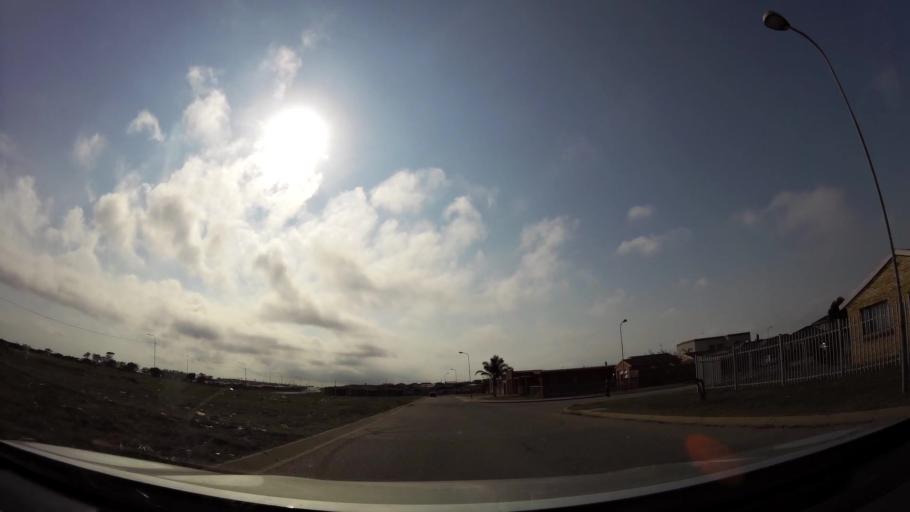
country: ZA
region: Eastern Cape
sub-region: Nelson Mandela Bay Metropolitan Municipality
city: Port Elizabeth
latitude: -33.9184
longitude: 25.5314
